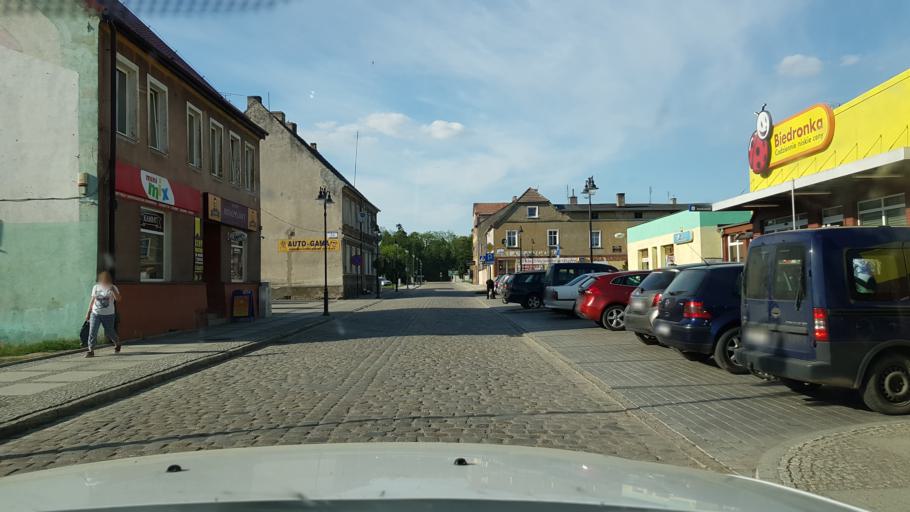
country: PL
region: West Pomeranian Voivodeship
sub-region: Powiat lobeski
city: Resko
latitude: 53.7732
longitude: 15.4062
